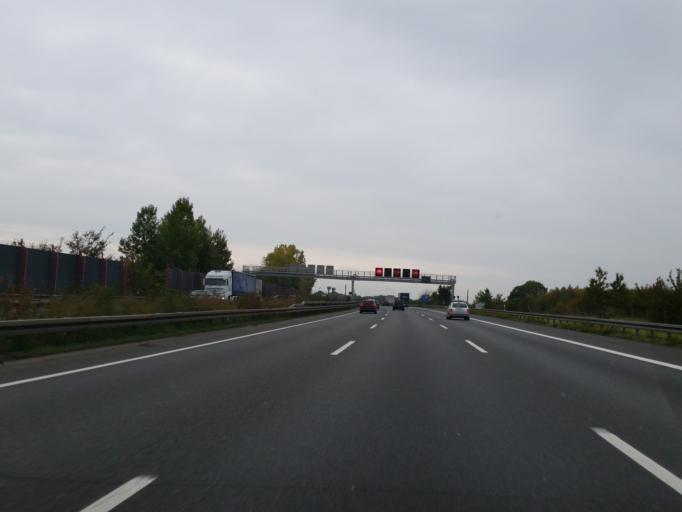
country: DE
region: Lower Saxony
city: Dollbergen
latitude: 52.3562
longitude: 10.1872
